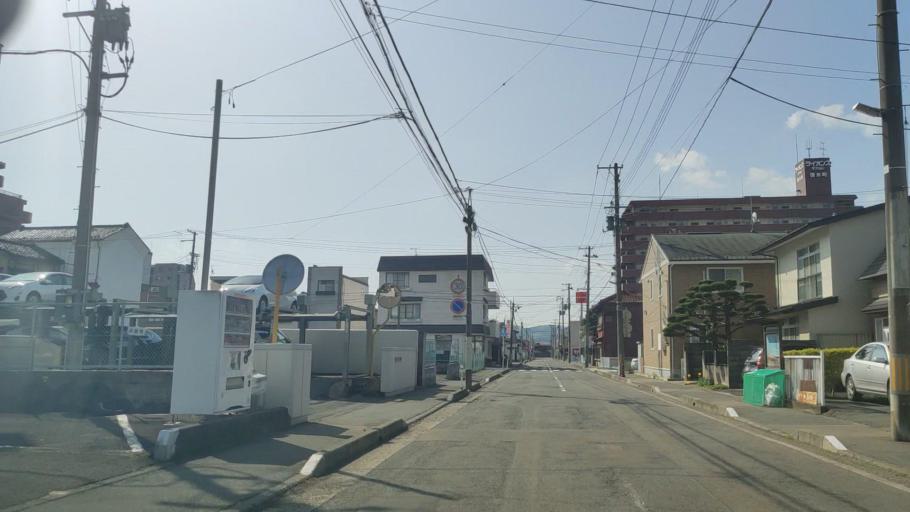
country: JP
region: Iwate
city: Morioka-shi
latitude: 39.6971
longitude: 141.1528
